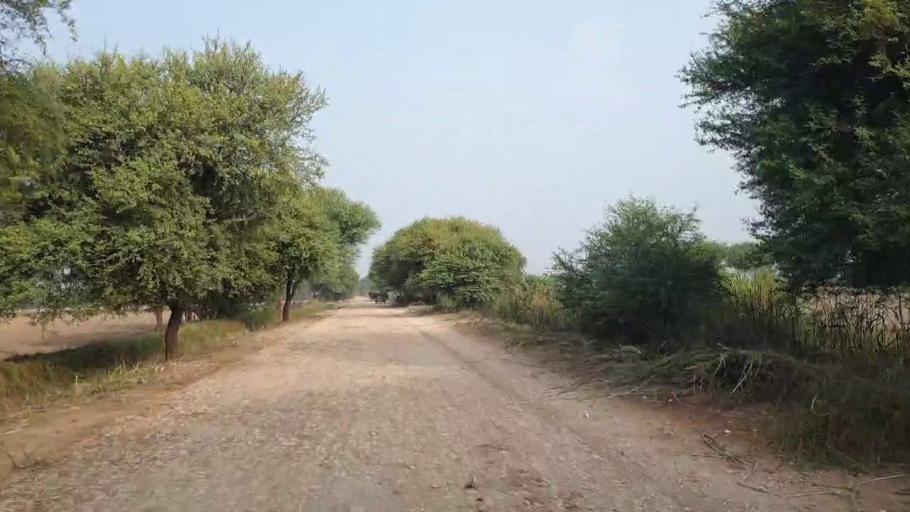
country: PK
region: Sindh
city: Tando Muhammad Khan
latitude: 25.1377
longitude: 68.5931
